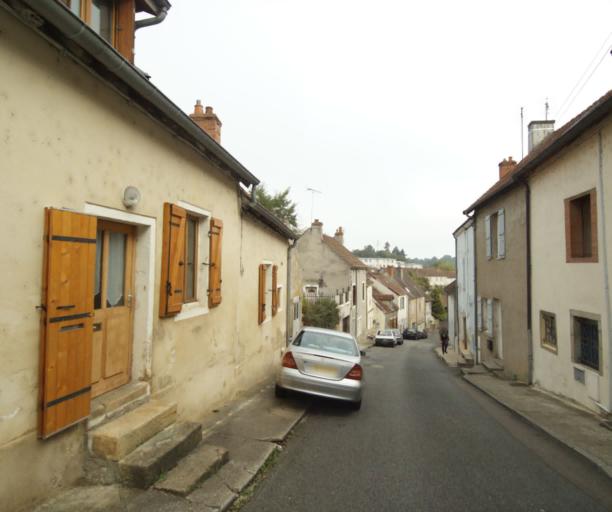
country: FR
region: Bourgogne
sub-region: Departement de Saone-et-Loire
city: Charolles
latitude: 46.4337
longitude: 4.2712
